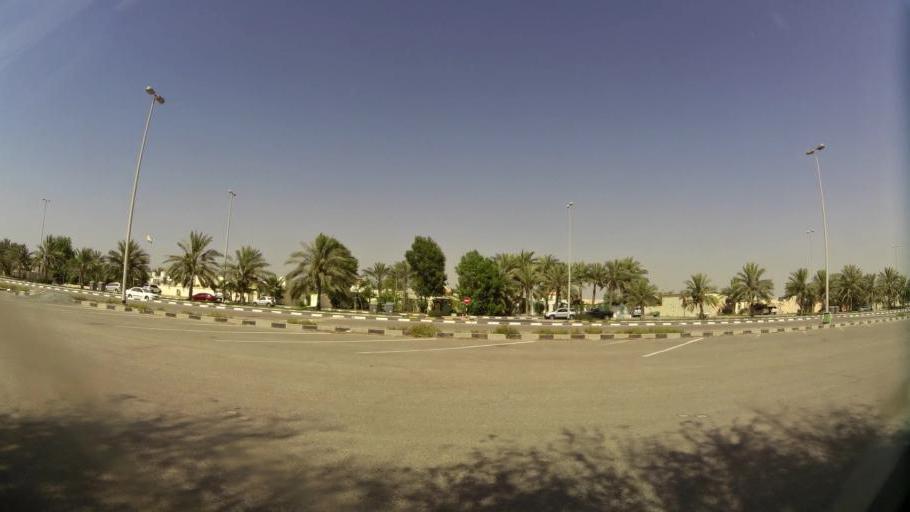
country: AE
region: Ajman
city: Ajman
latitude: 25.4169
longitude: 55.4711
